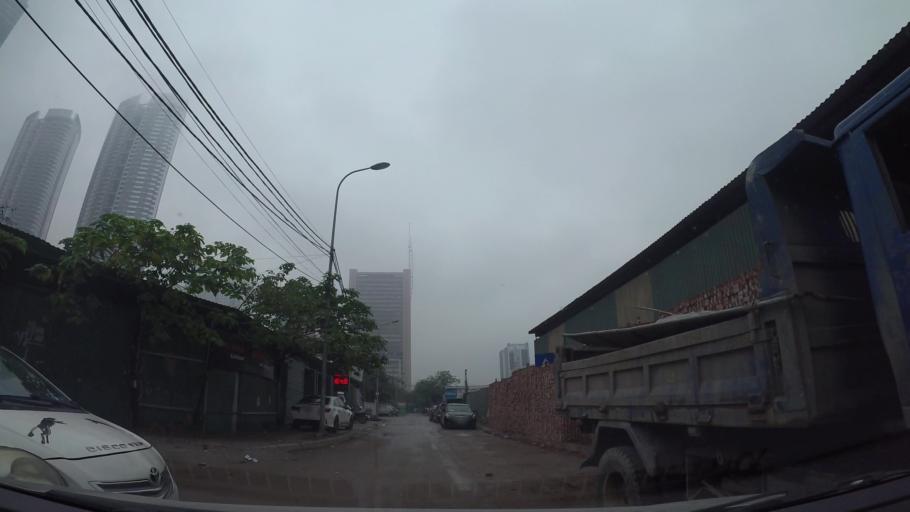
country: VN
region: Ha Noi
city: Cau Giay
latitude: 21.0177
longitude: 105.7871
